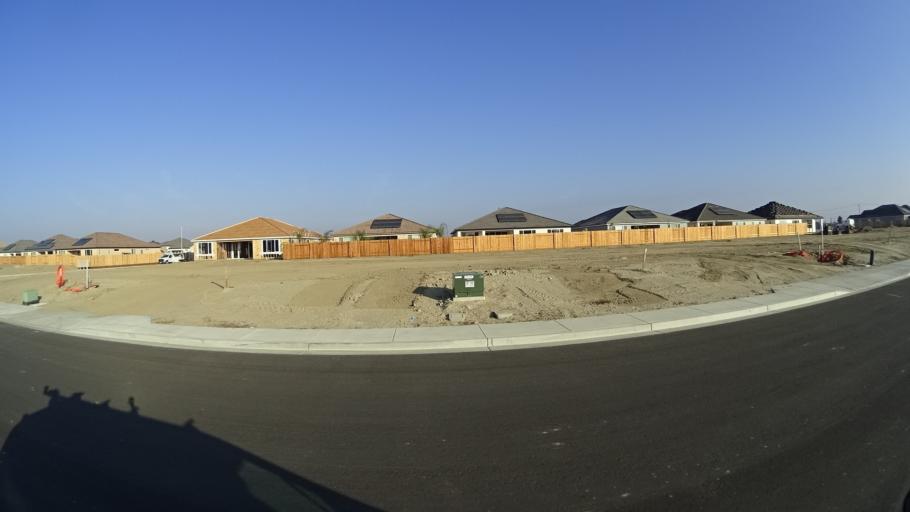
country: US
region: California
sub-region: Kern County
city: Greenacres
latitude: 35.2928
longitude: -119.1120
